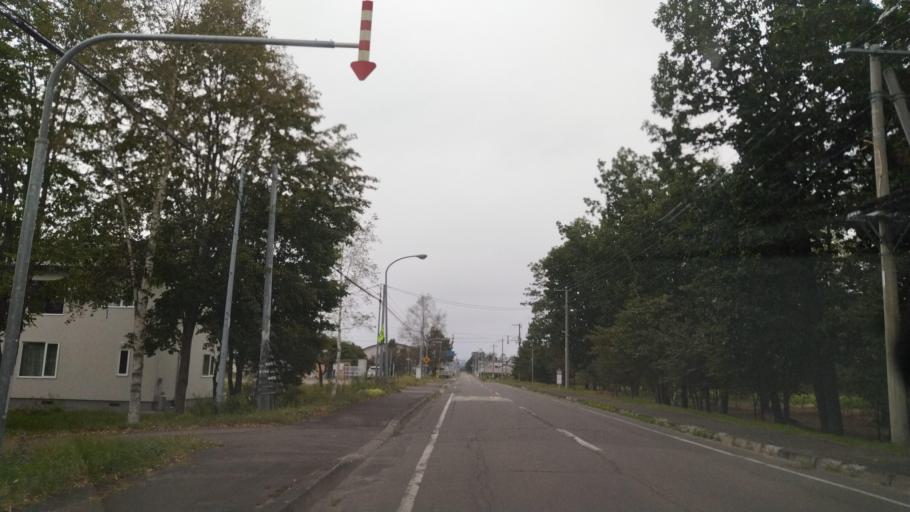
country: JP
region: Hokkaido
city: Otofuke
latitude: 43.2286
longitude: 143.2793
